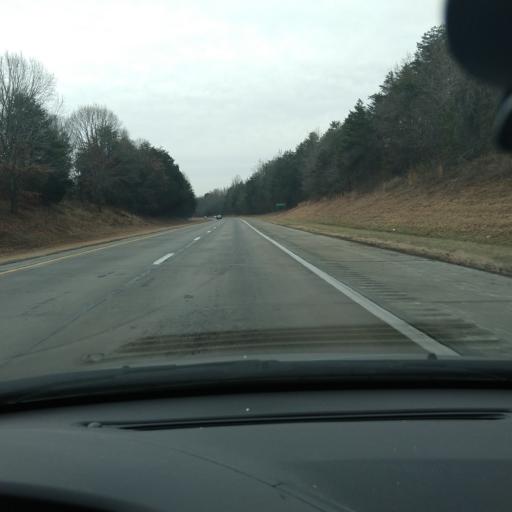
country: US
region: North Carolina
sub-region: Davidson County
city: Midway
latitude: 35.9978
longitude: -80.2381
